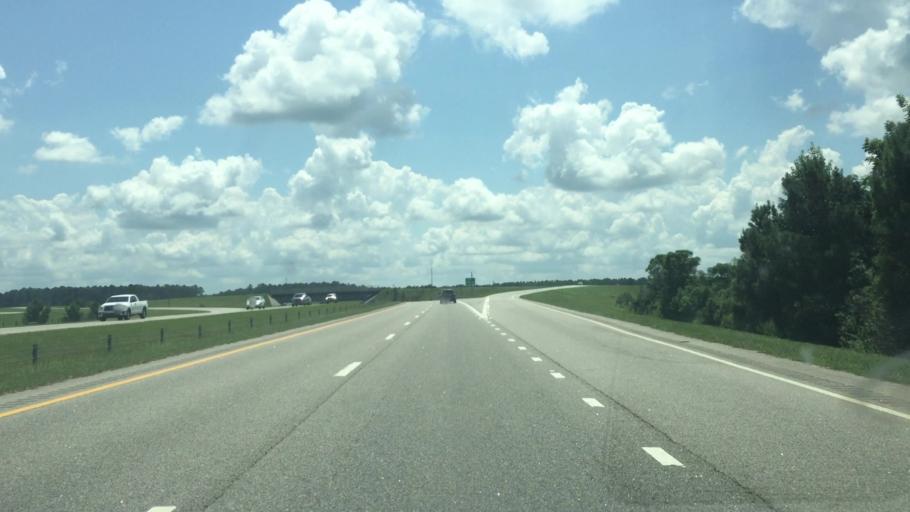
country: US
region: North Carolina
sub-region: Robeson County
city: Pembroke
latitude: 34.6076
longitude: -79.2044
